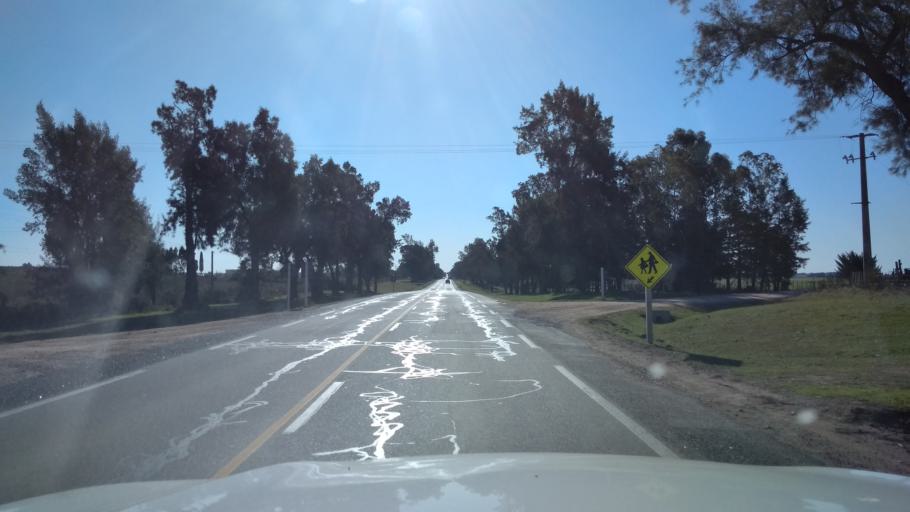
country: UY
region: Canelones
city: San Jacinto
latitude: -34.5893
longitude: -55.8371
